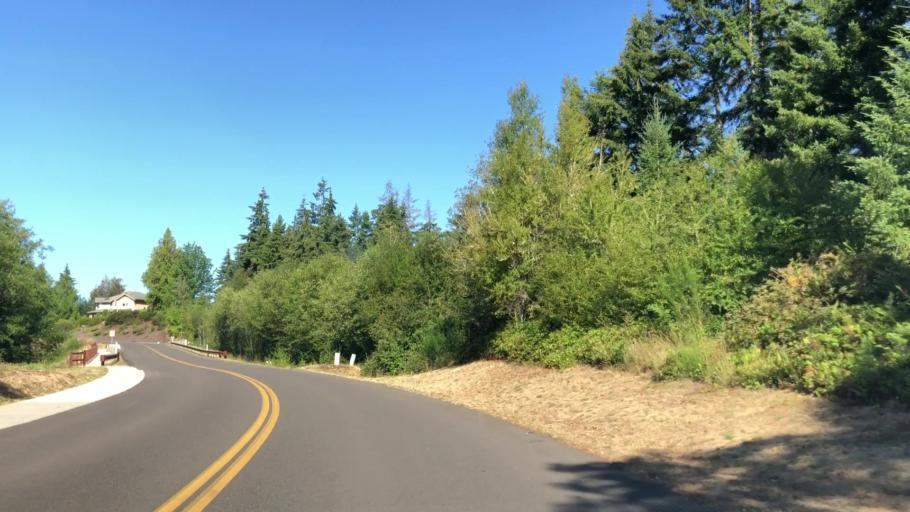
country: US
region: Washington
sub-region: Kitsap County
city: Indianola
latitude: 47.7727
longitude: -122.5213
